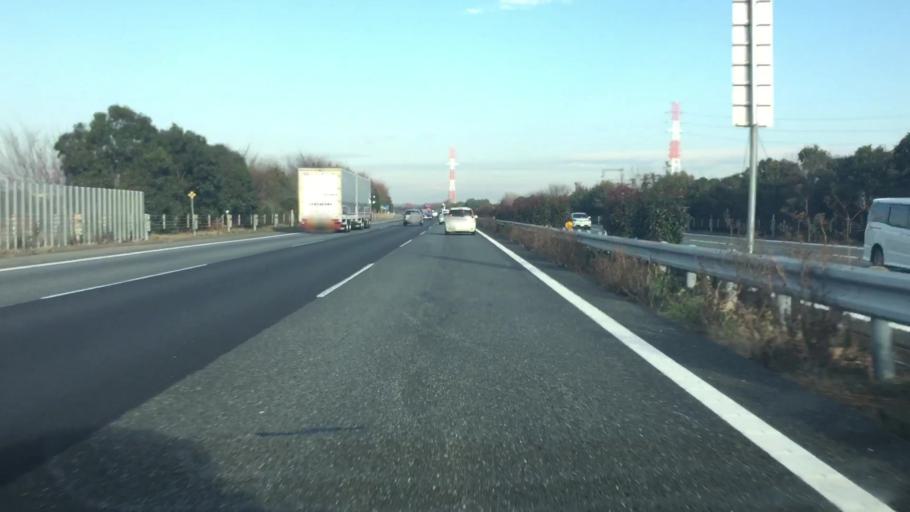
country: JP
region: Saitama
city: Yorii
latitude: 36.1461
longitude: 139.2225
